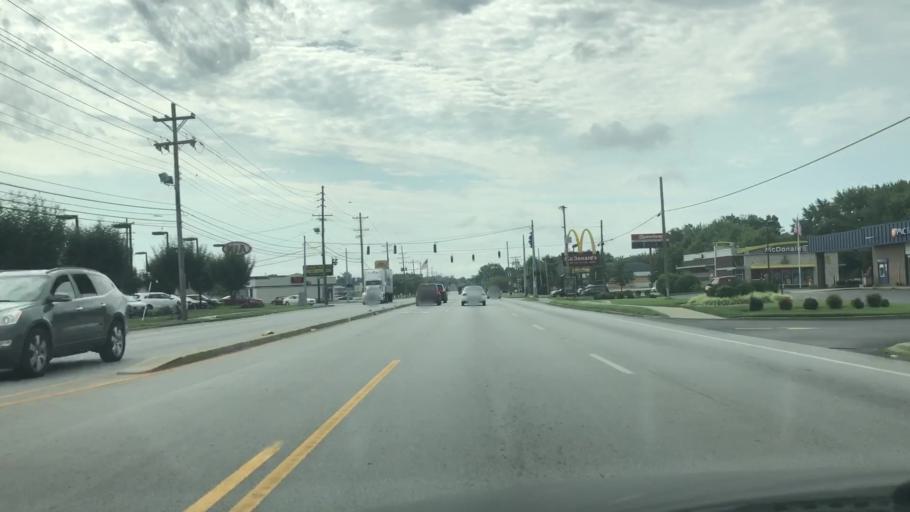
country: US
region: Kentucky
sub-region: Jefferson County
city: Okolona
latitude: 38.1695
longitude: -85.7074
